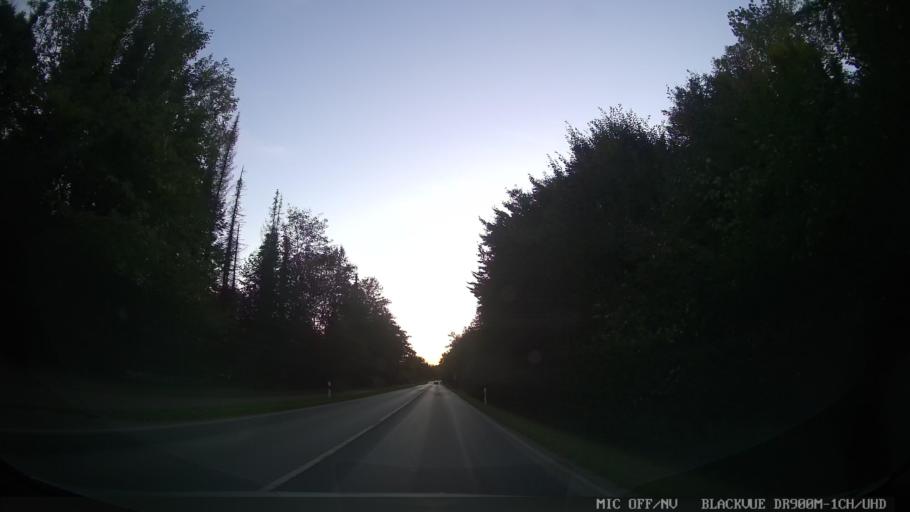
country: DE
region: Schleswig-Holstein
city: Susel
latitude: 54.0874
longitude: 10.7300
